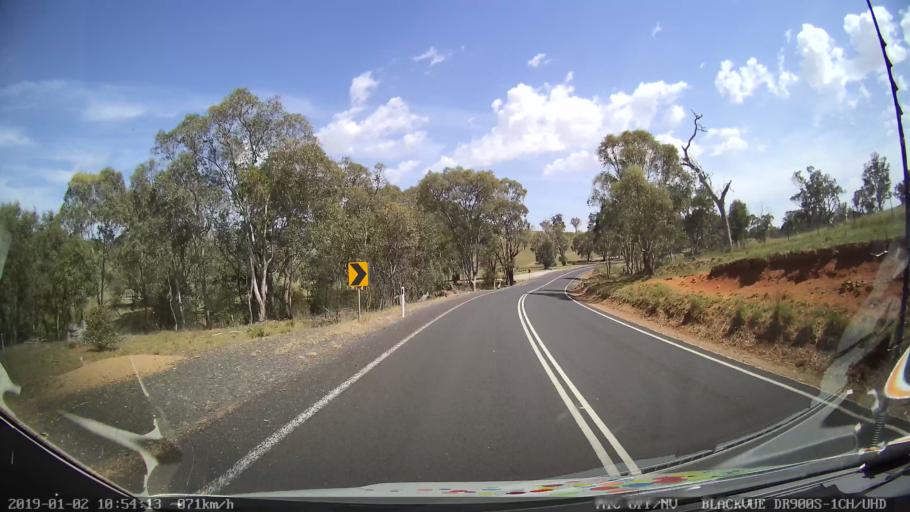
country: AU
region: New South Wales
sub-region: Cootamundra
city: Cootamundra
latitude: -34.6722
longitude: 148.2734
